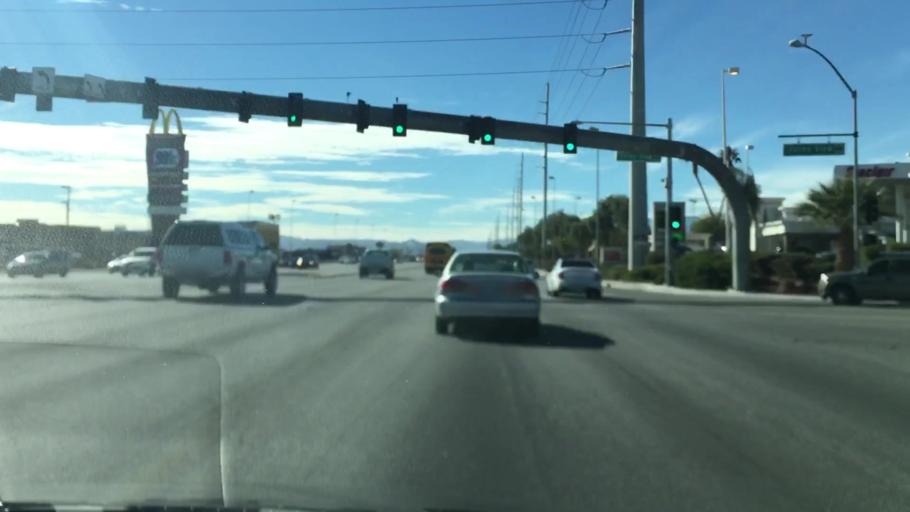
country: US
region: Nevada
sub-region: Clark County
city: Enterprise
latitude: 36.0407
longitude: -115.1901
